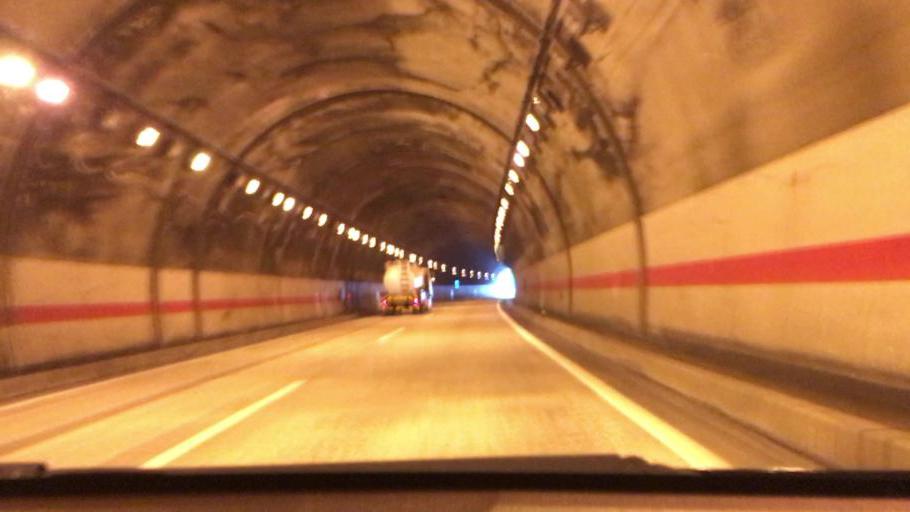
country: JP
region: Yamaguchi
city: Tokuyama
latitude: 34.0663
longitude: 131.6940
